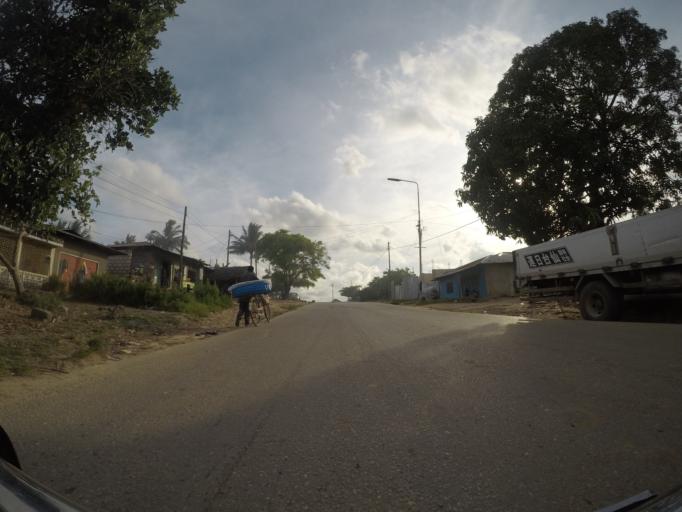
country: TZ
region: Pemba South
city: Chake Chake
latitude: -5.2584
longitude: 39.7747
